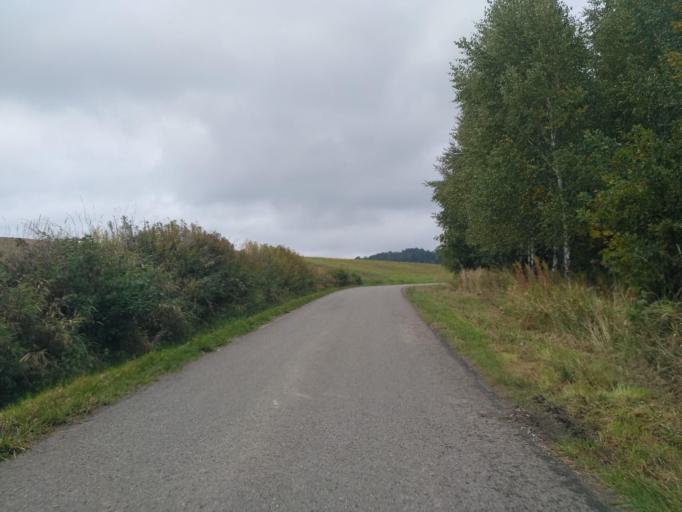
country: PL
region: Subcarpathian Voivodeship
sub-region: Powiat debicki
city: Brzostek
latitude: 49.9382
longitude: 21.4542
